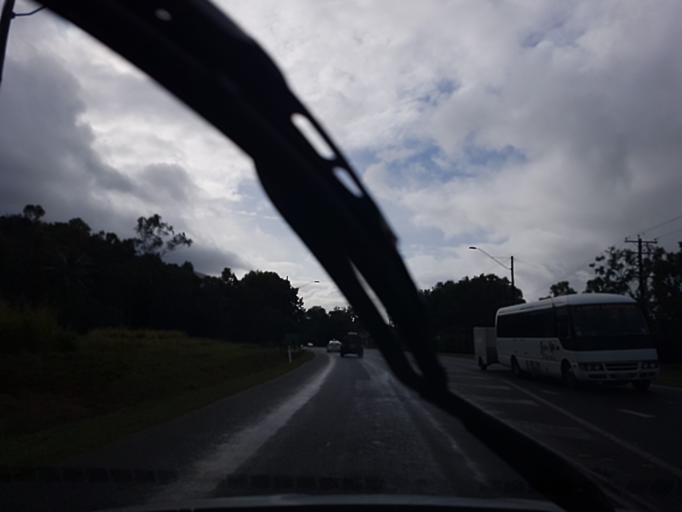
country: AU
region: Queensland
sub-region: Cairns
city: Palm Cove
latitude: -16.7741
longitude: 145.6749
